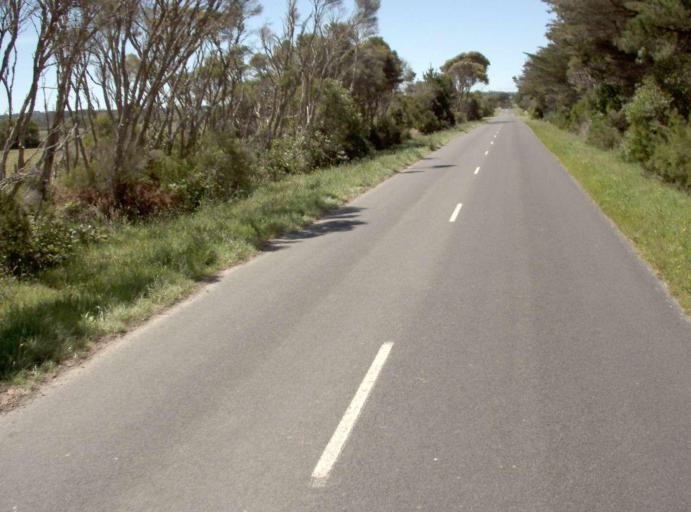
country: AU
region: Victoria
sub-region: Bass Coast
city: North Wonthaggi
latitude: -38.8009
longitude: 146.0858
